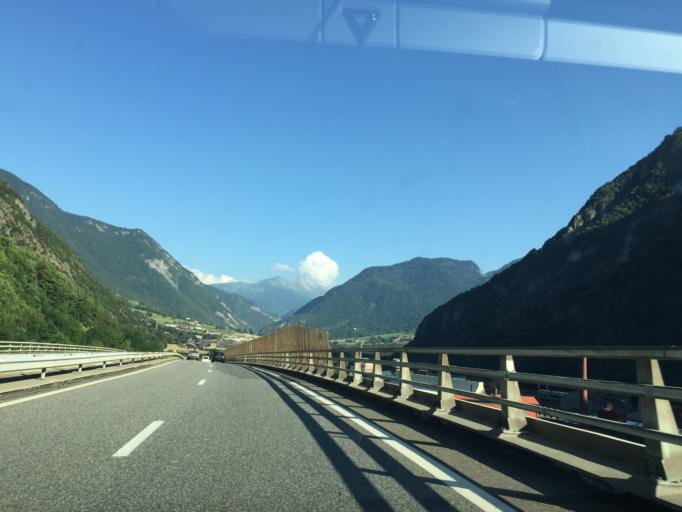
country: FR
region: Rhone-Alpes
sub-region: Departement de la Savoie
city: Aigueblanche
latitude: 45.5314
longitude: 6.4756
